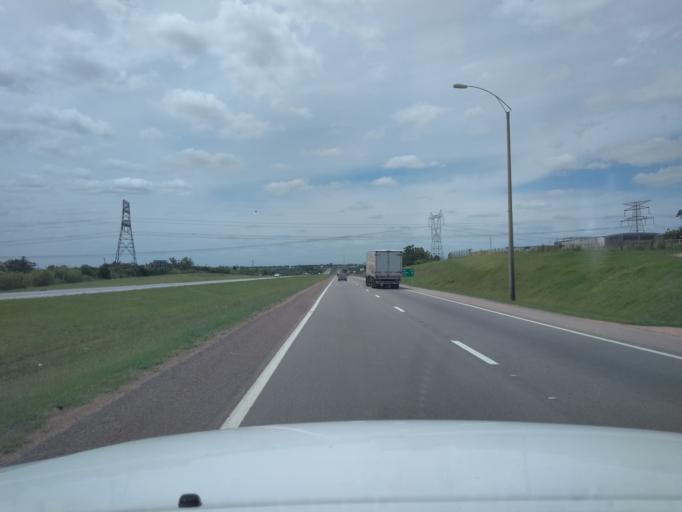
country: UY
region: Canelones
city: La Paz
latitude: -34.7643
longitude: -56.2642
